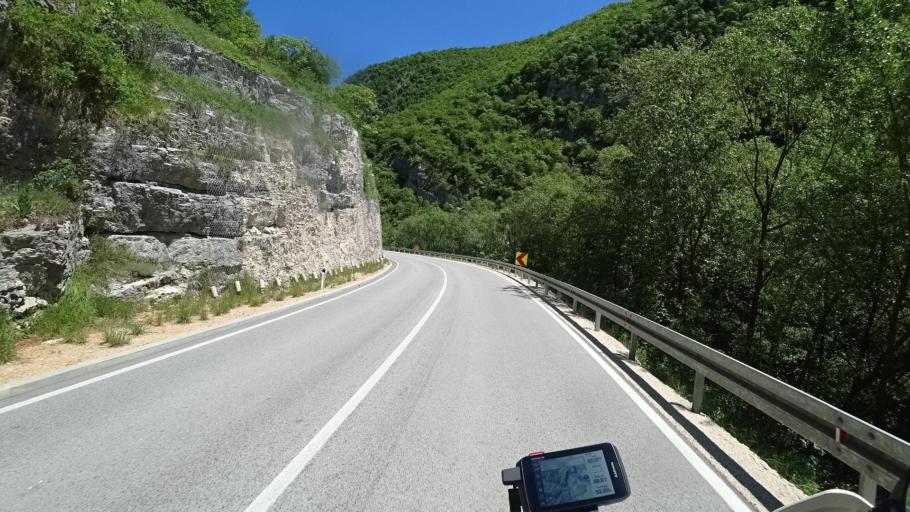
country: BA
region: Republika Srpska
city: Mrkonjic Grad
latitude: 44.4595
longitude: 17.1616
